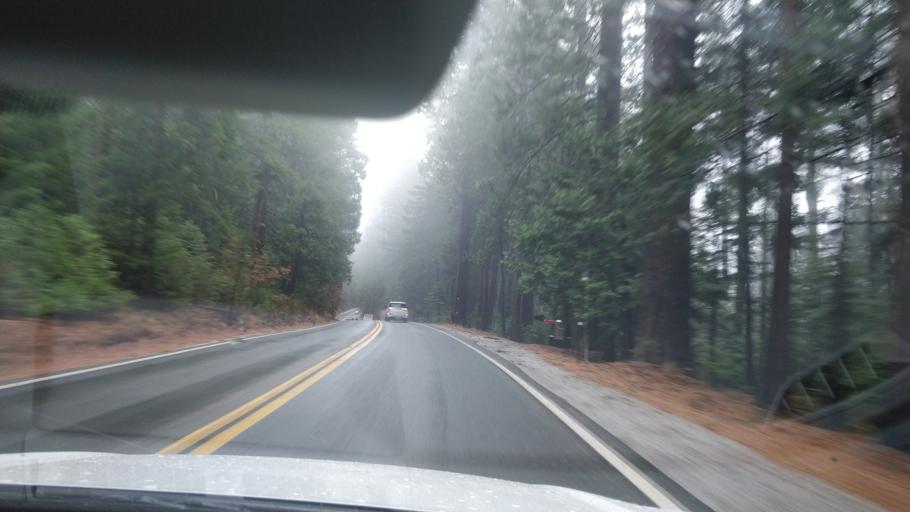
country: US
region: California
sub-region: Nevada County
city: Nevada City
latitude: 39.3224
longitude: -120.8590
